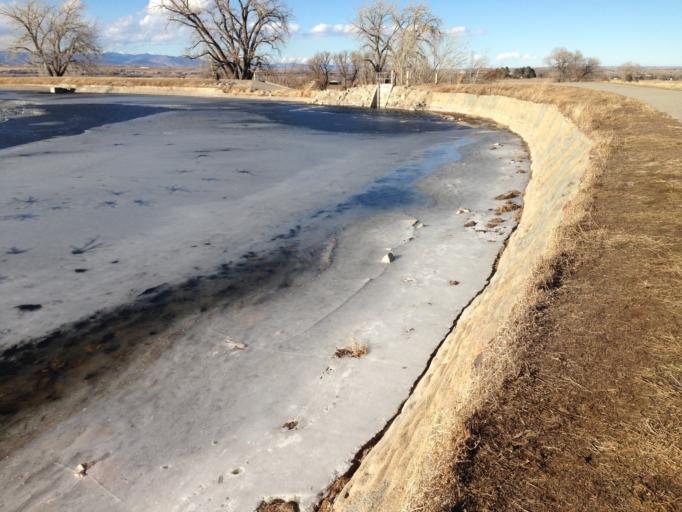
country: US
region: Colorado
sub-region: Boulder County
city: Lafayette
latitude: 40.0187
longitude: -105.0967
